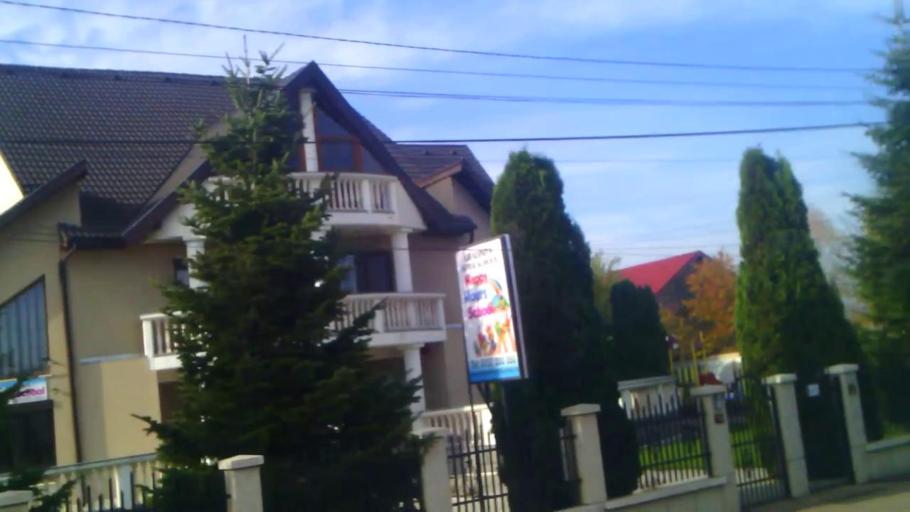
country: RO
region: Ilfov
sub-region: Comuna Berceni
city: Berceni
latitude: 44.3300
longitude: 26.1729
